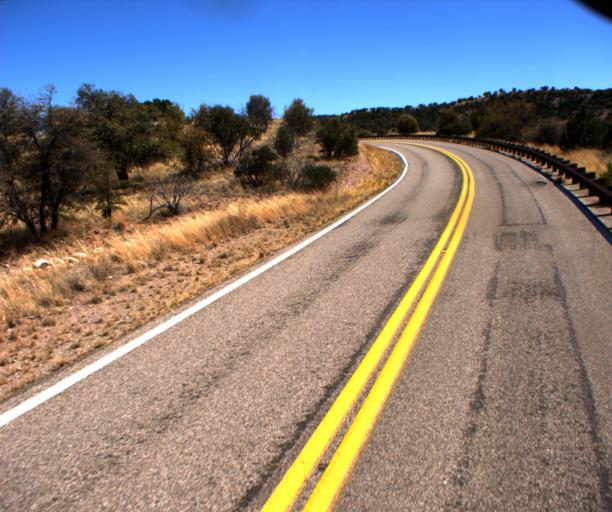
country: US
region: Arizona
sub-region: Cochise County
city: Sierra Vista
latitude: 31.4918
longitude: -110.4901
